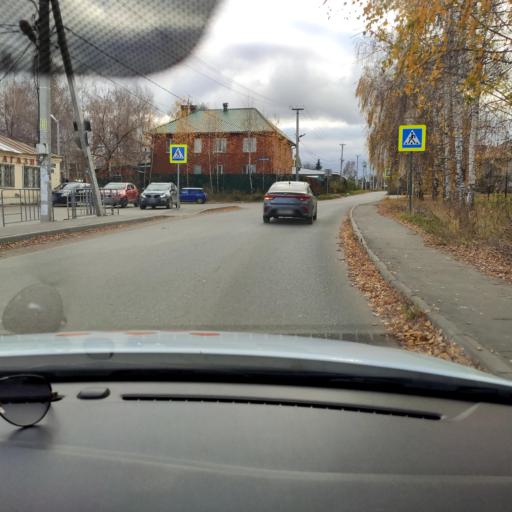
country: RU
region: Tatarstan
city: Stolbishchi
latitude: 55.7414
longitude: 49.2731
